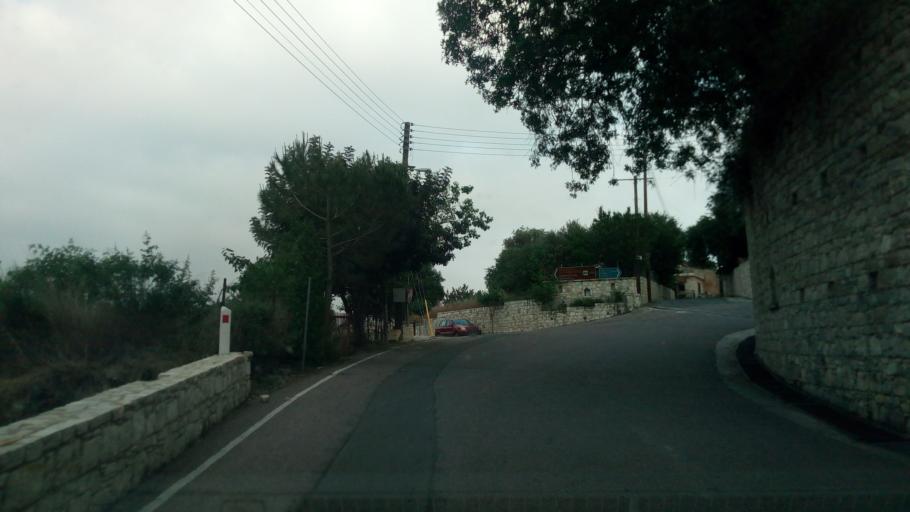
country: CY
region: Limassol
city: Pachna
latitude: 34.8398
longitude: 32.6894
